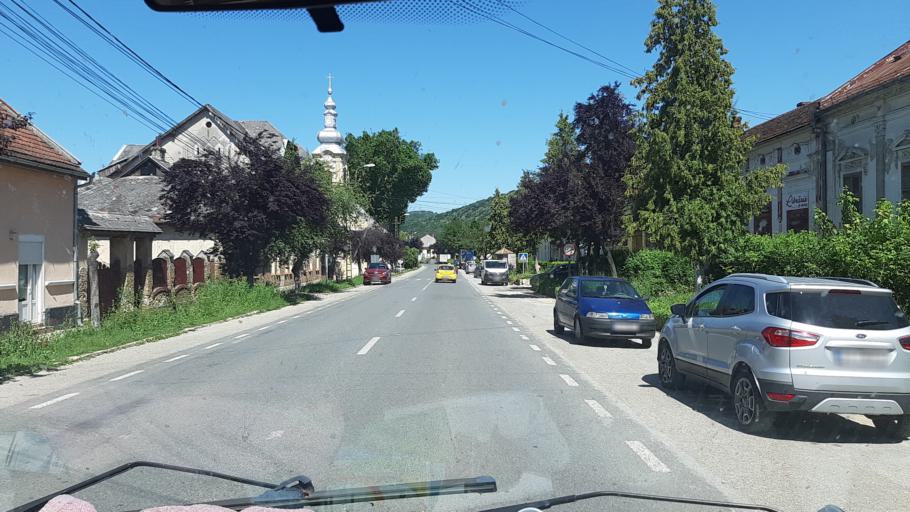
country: RO
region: Caras-Severin
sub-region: Oras Bocsa
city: Bocsa
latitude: 45.3800
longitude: 21.7764
